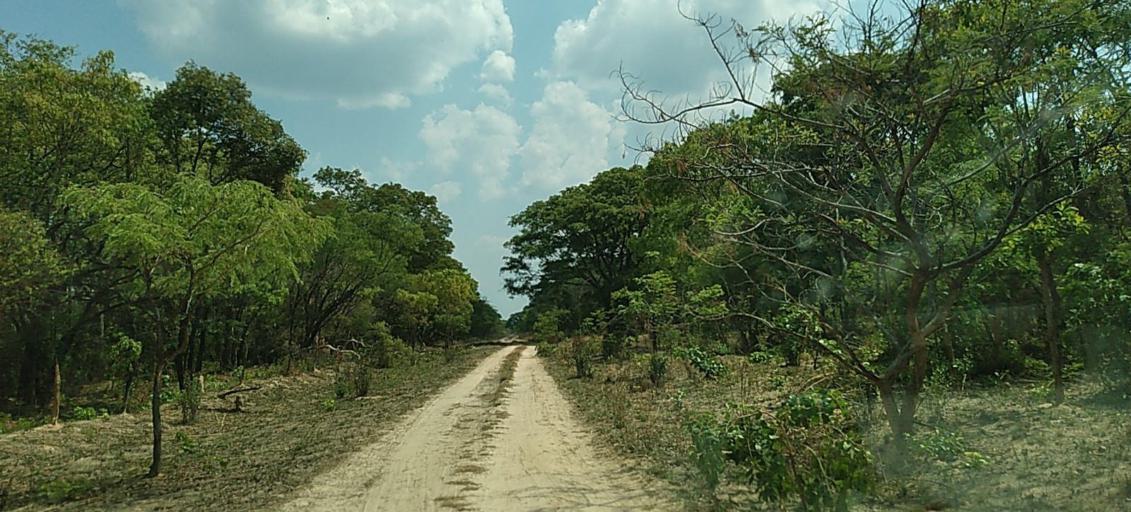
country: ZM
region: Copperbelt
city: Mpongwe
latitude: -13.8424
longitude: 27.9350
